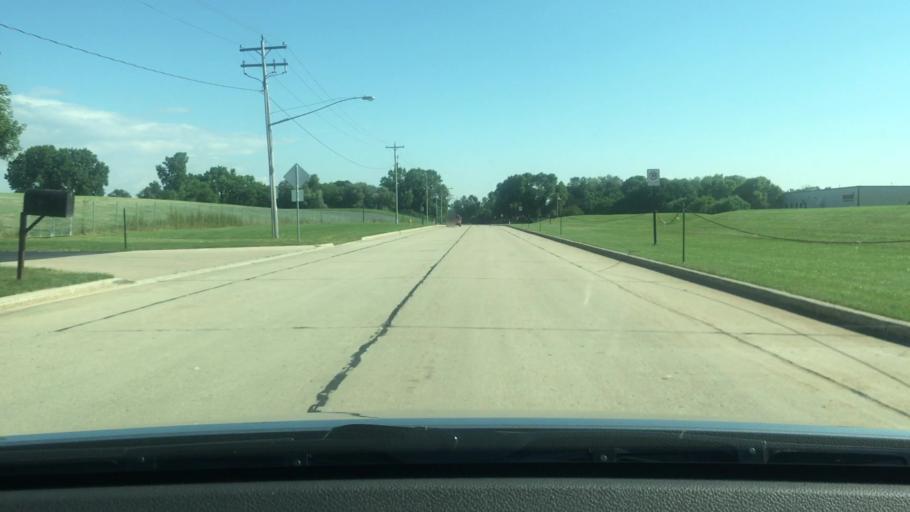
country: US
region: Wisconsin
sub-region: Winnebago County
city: Oshkosh
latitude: 43.9757
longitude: -88.5497
